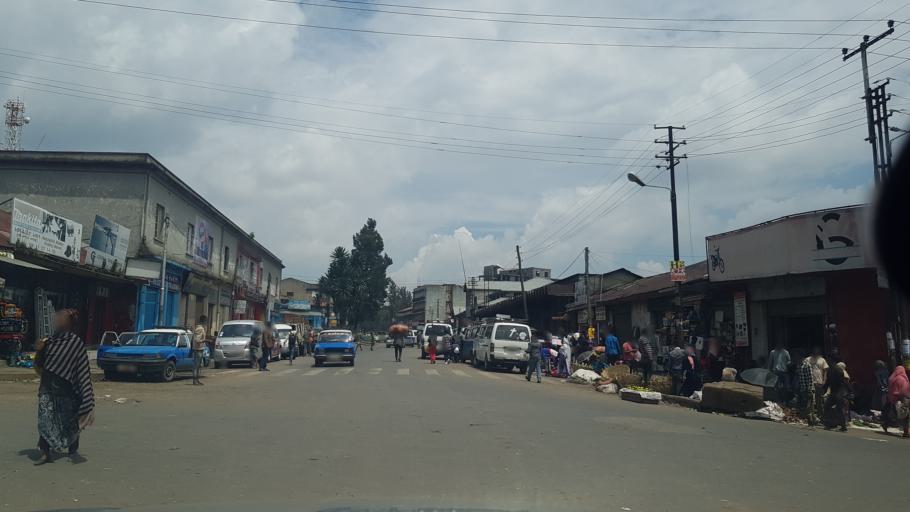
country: ET
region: Adis Abeba
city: Addis Ababa
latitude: 9.0337
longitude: 38.7491
